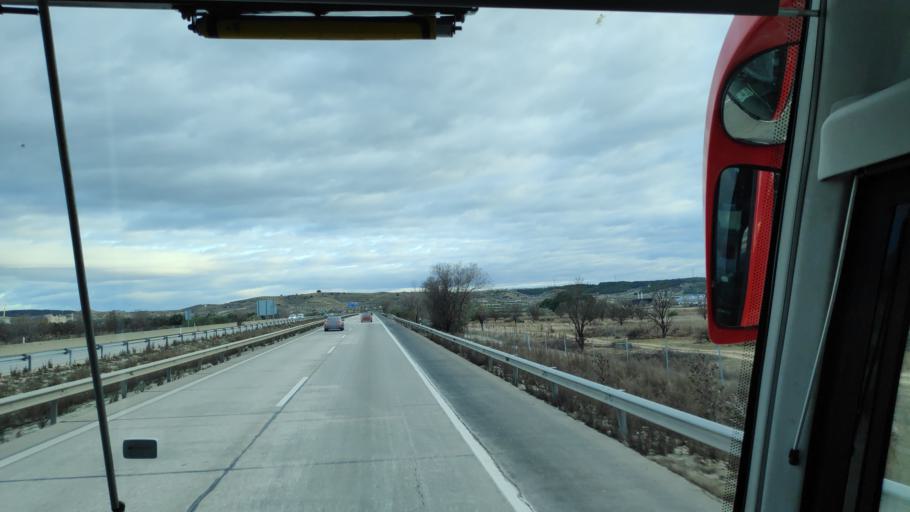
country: ES
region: Madrid
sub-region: Provincia de Madrid
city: Vaciamadrid
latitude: 40.3038
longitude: -3.4870
